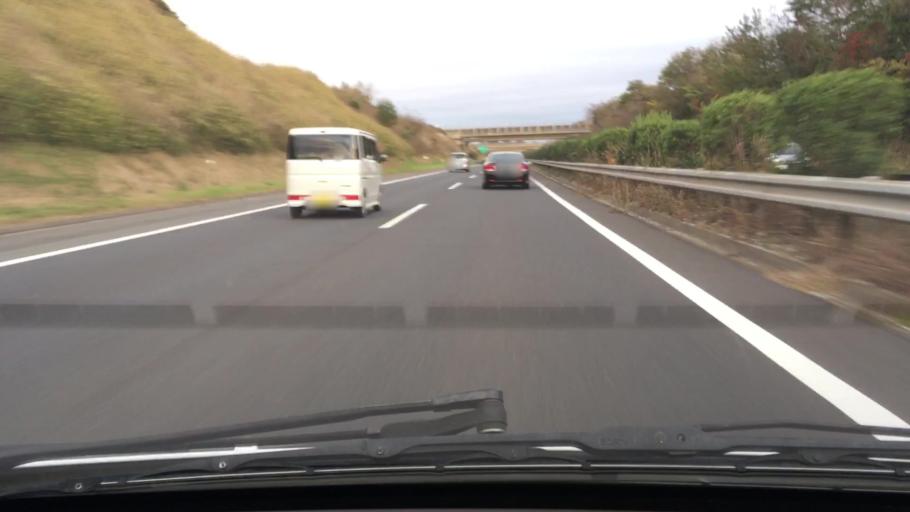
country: JP
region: Chiba
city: Ichihara
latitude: 35.4248
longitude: 140.0261
